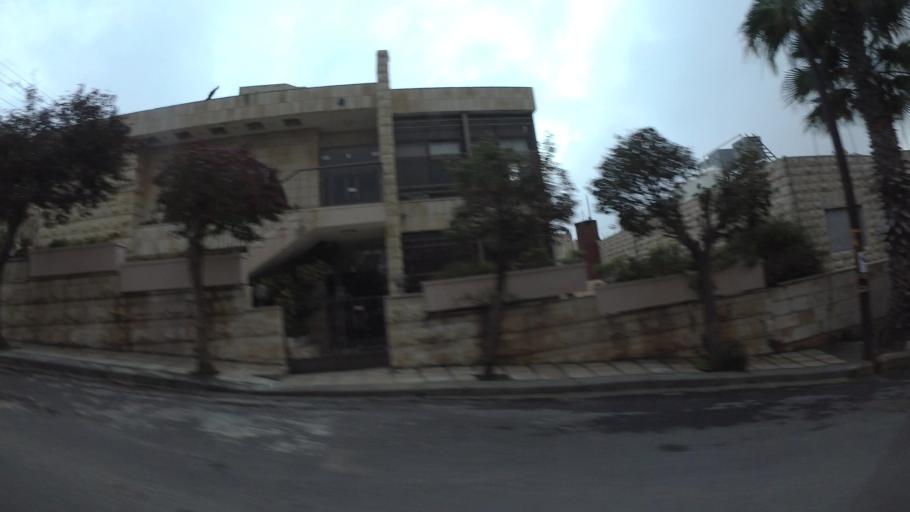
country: JO
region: Amman
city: Al Jubayhah
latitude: 31.9676
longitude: 35.8835
